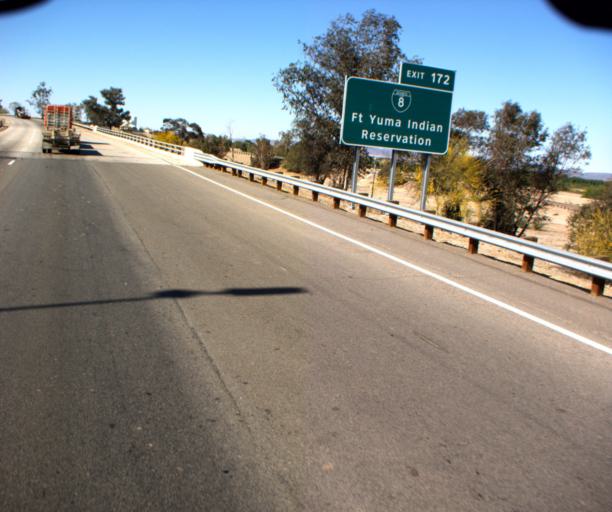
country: US
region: Arizona
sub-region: Yuma County
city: Yuma
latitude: 32.7213
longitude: -114.6130
